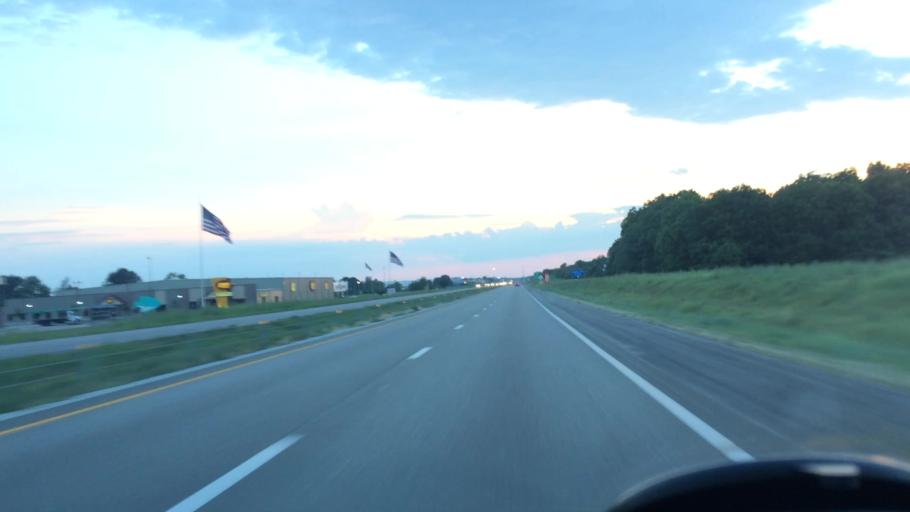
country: US
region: Missouri
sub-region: Greene County
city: Strafford
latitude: 37.2503
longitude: -93.1944
